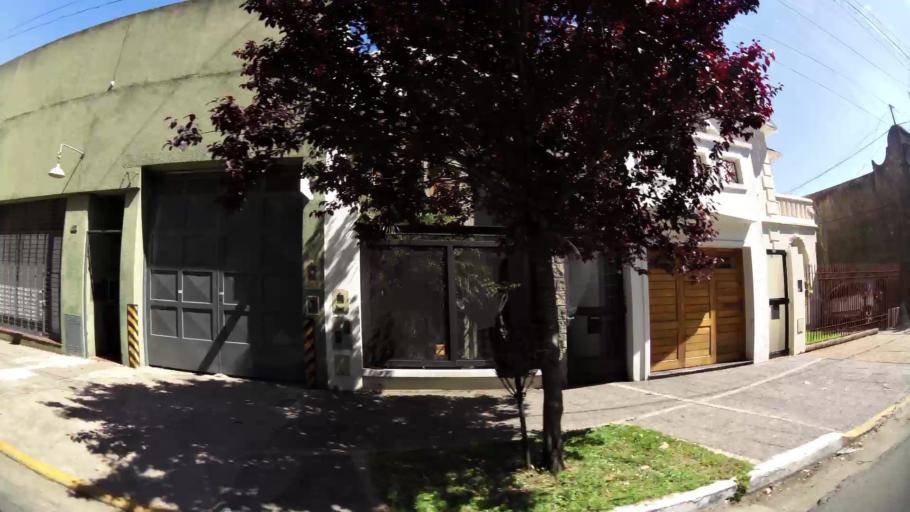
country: AR
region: Buenos Aires
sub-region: Partido de Quilmes
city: Quilmes
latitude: -34.7119
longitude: -58.2864
